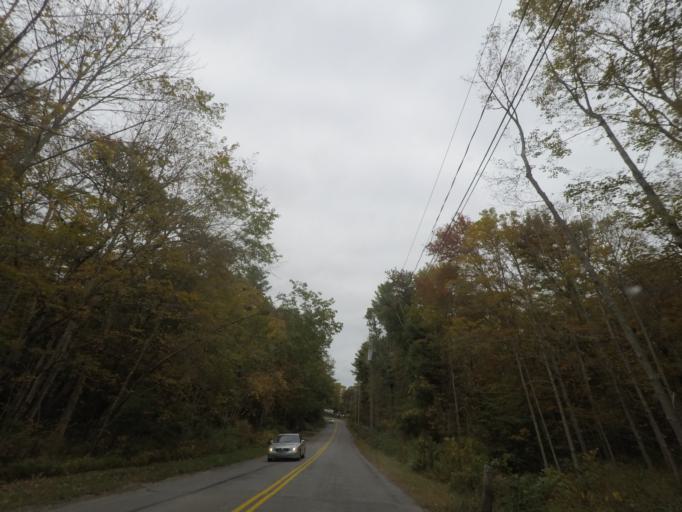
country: US
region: Connecticut
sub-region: Windham County
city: Thompson
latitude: 41.9460
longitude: -71.8355
